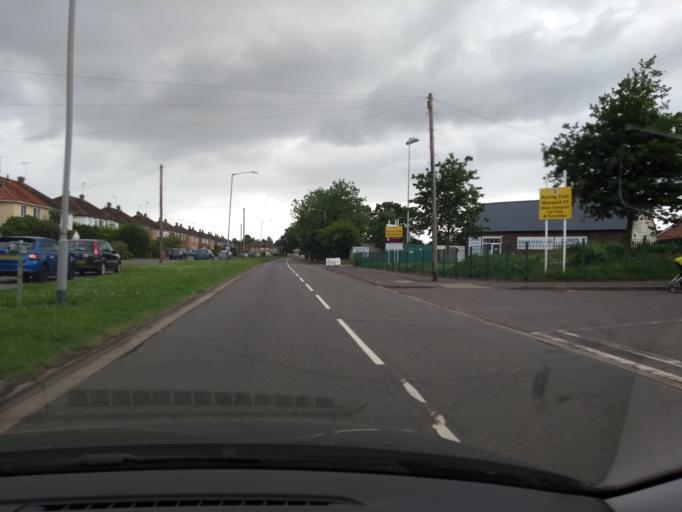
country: GB
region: England
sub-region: Warwickshire
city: Warwick
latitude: 52.2760
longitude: -1.6000
